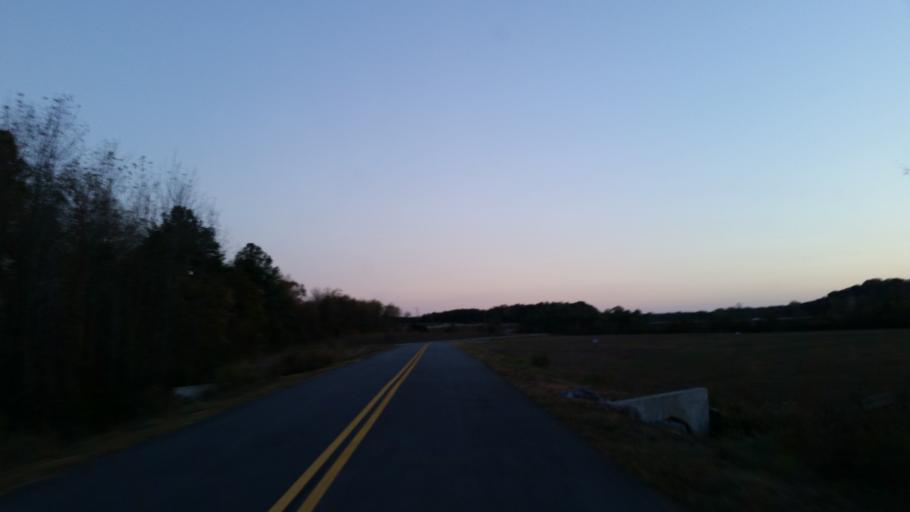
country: US
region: Georgia
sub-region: Gordon County
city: Calhoun
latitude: 34.5831
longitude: -84.9532
